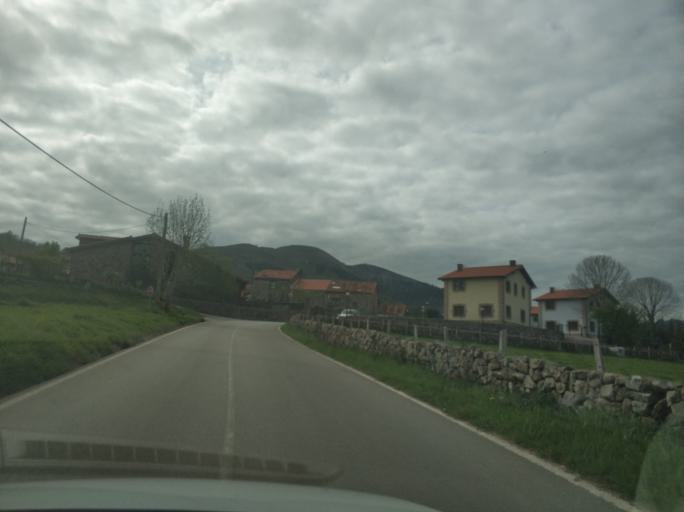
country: ES
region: Cantabria
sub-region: Provincia de Cantabria
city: Ruente
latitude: 43.2352
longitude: -4.2822
